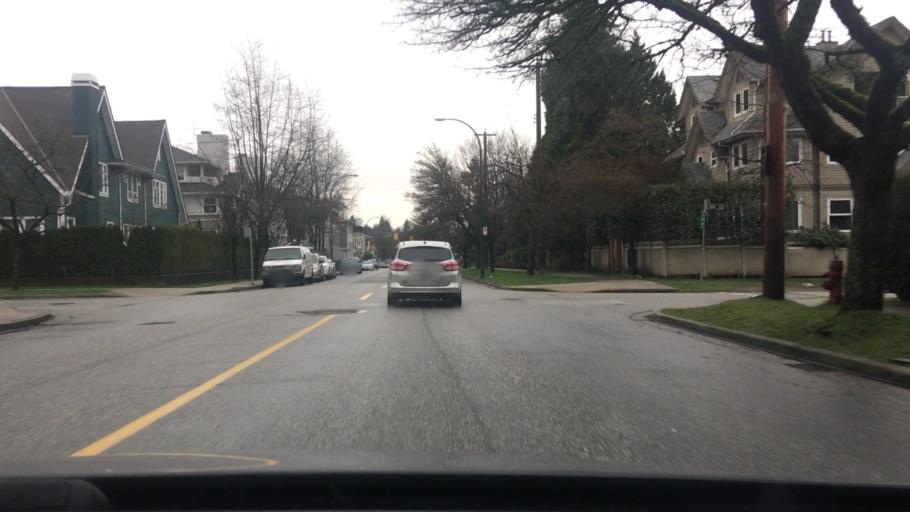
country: CA
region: British Columbia
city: Vancouver
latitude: 49.2570
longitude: -123.1177
